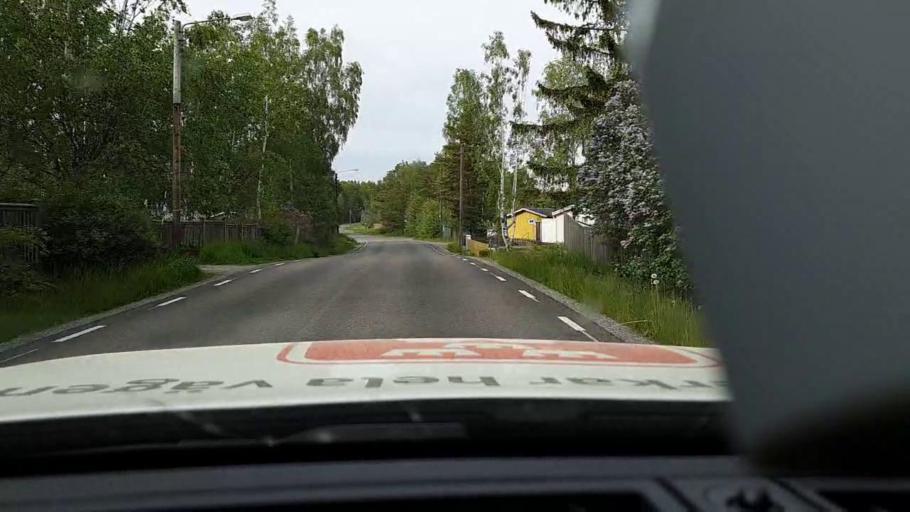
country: SE
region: Stockholm
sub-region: Haninge Kommun
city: Haninge
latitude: 59.0866
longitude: 18.1783
